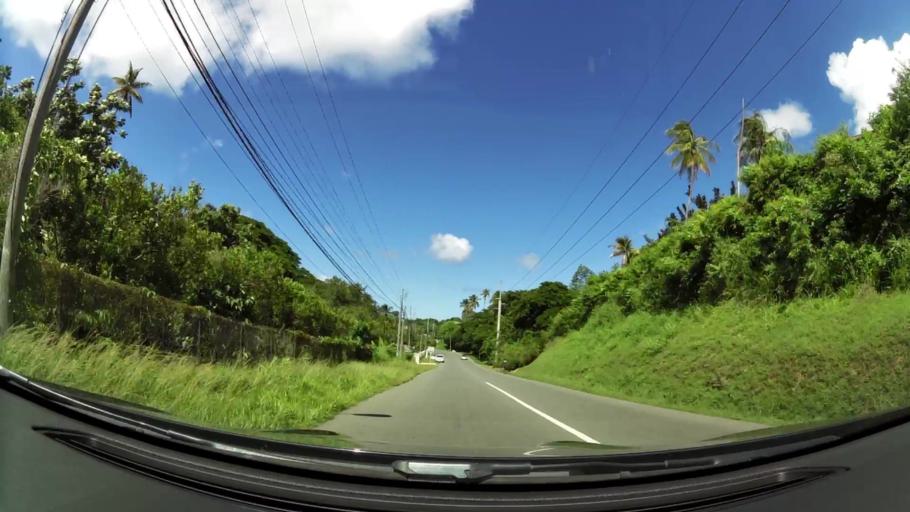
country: TT
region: Tobago
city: Scarborough
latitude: 11.1915
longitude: -60.7953
